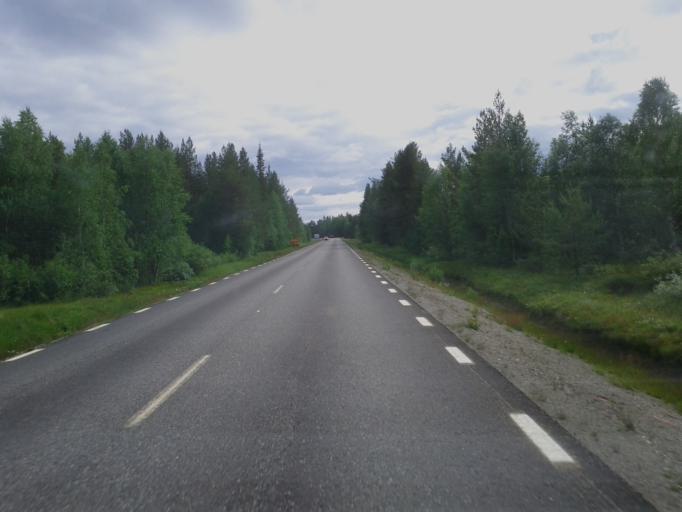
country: SE
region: Vaesterbotten
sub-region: Sorsele Kommun
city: Sorsele
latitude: 65.2785
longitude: 17.6663
